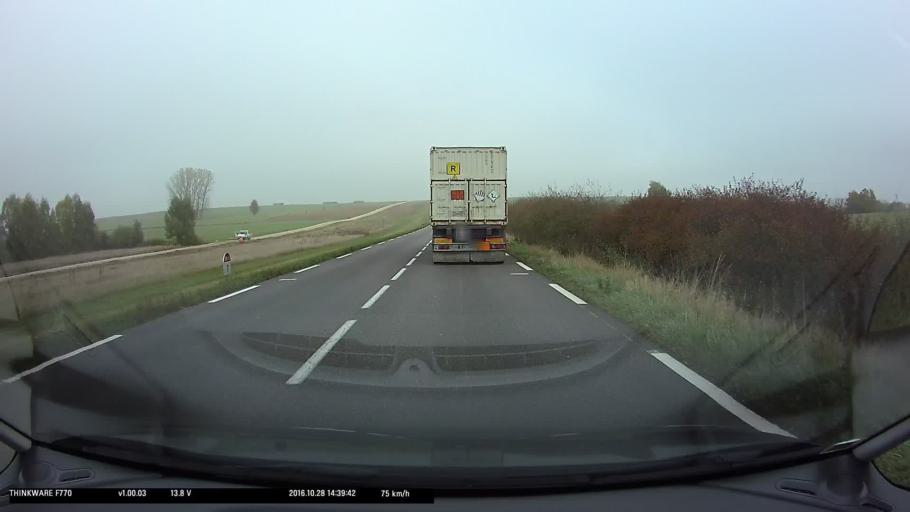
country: FR
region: Lorraine
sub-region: Departement de la Moselle
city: Lorquin
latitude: 48.6702
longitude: 6.9438
